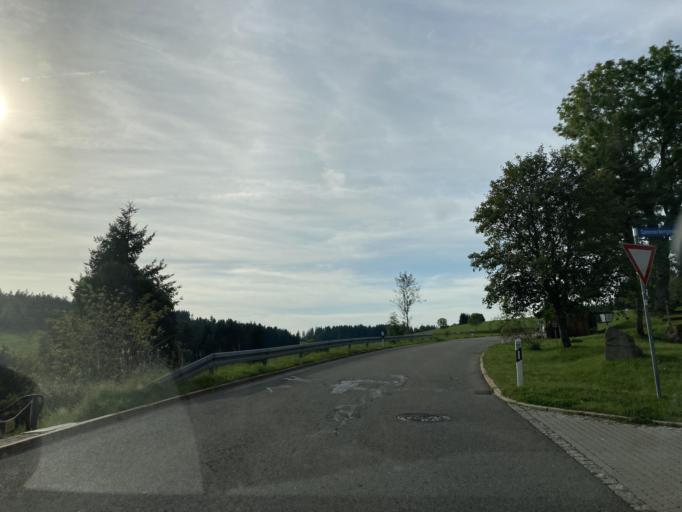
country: DE
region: Baden-Wuerttemberg
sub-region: Freiburg Region
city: Titisee-Neustadt
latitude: 47.9815
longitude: 8.1640
